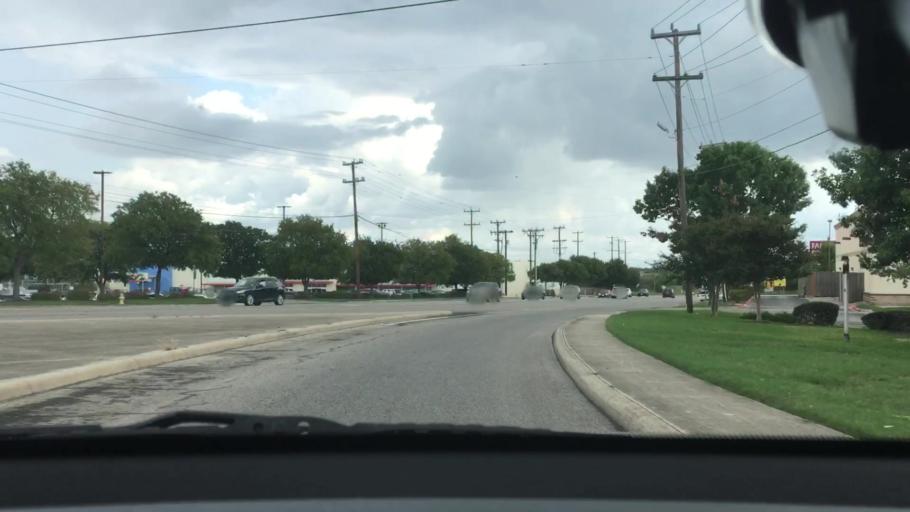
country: US
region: Texas
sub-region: Bexar County
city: Windcrest
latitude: 29.5101
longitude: -98.3718
